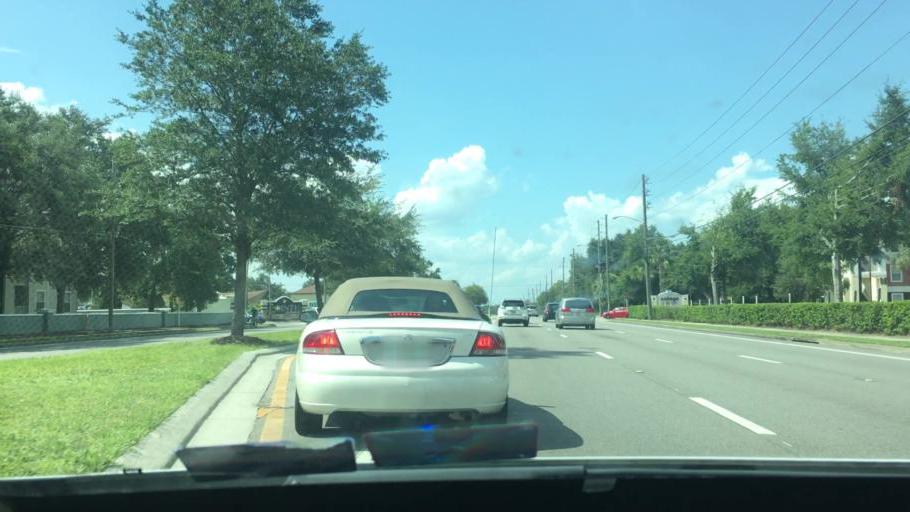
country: US
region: Florida
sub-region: Orange County
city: Alafaya
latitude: 28.5786
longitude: -81.2077
